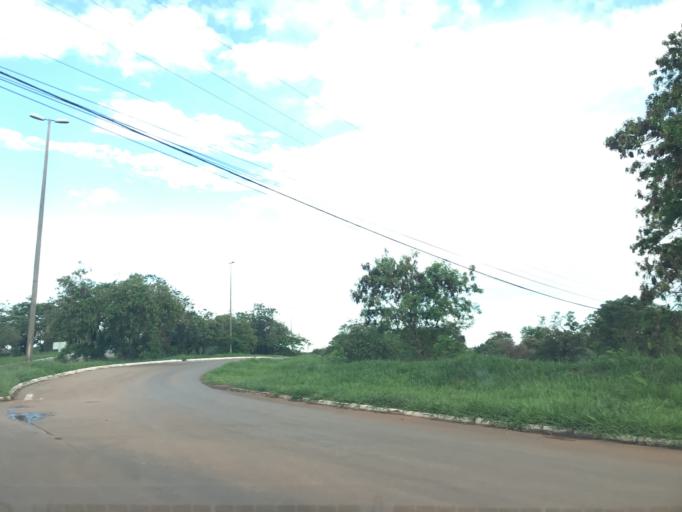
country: BR
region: Federal District
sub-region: Brasilia
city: Brasilia
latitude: -15.8314
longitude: -47.9034
